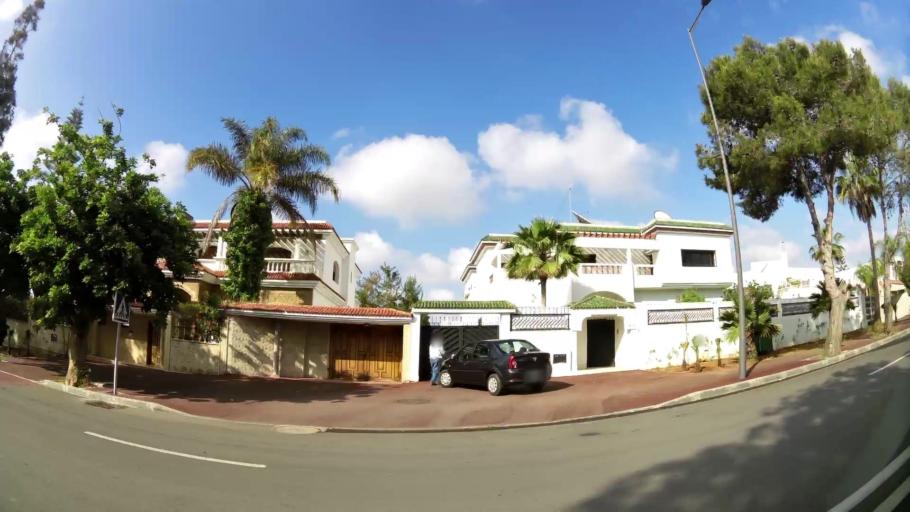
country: MA
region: Rabat-Sale-Zemmour-Zaer
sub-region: Skhirate-Temara
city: Temara
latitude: 33.9595
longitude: -6.8623
